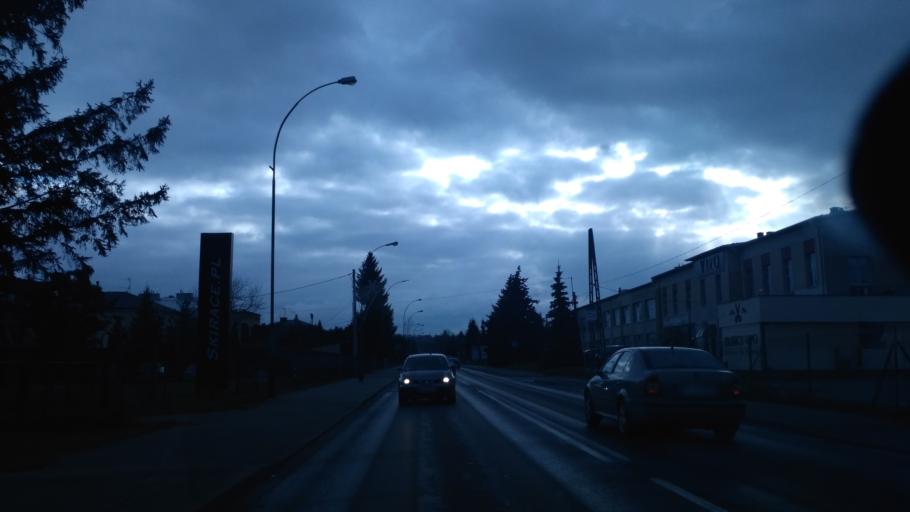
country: PL
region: Subcarpathian Voivodeship
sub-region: Powiat lancucki
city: Lancut
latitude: 50.0886
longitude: 22.2320
